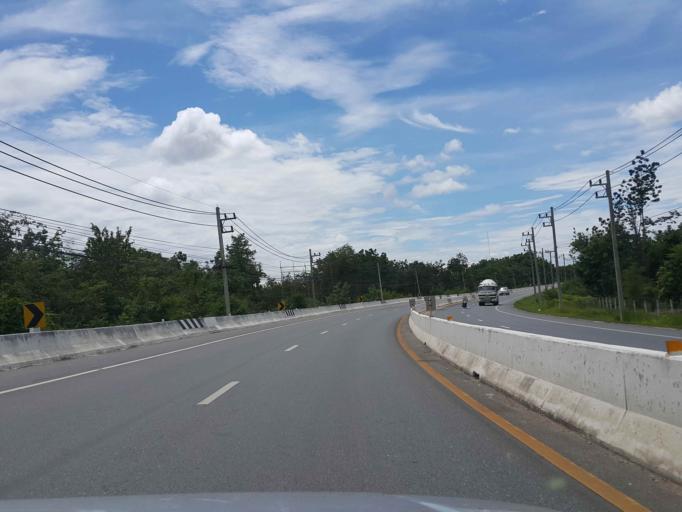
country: TH
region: Sukhothai
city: Ban Dan Lan Hoi
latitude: 17.0000
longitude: 99.5347
